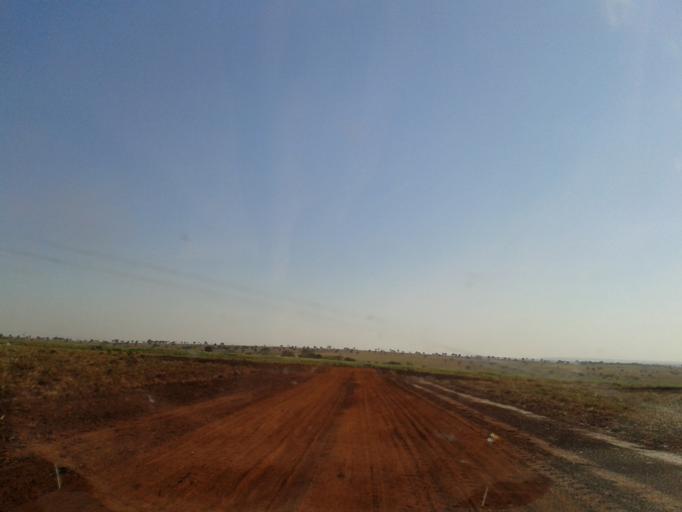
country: BR
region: Minas Gerais
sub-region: Santa Vitoria
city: Santa Vitoria
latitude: -18.7347
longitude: -50.2603
